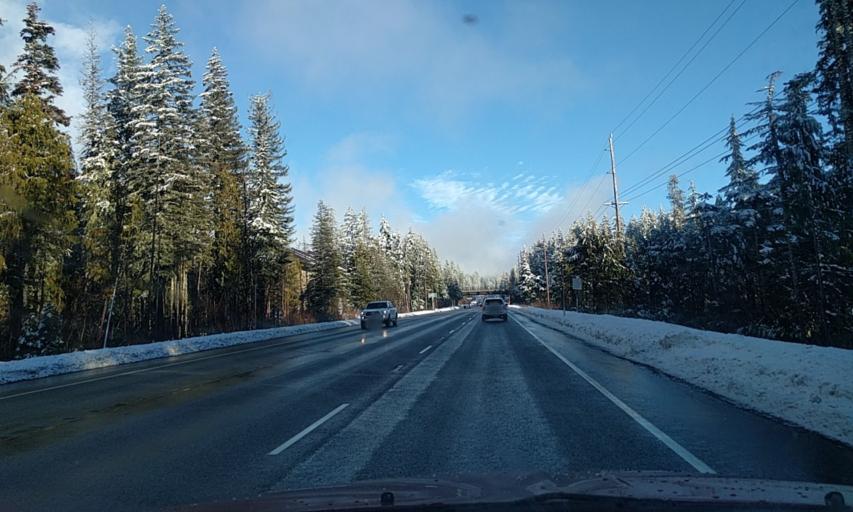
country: US
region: Oregon
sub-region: Clackamas County
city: Mount Hood Village
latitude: 45.3026
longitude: -121.7613
